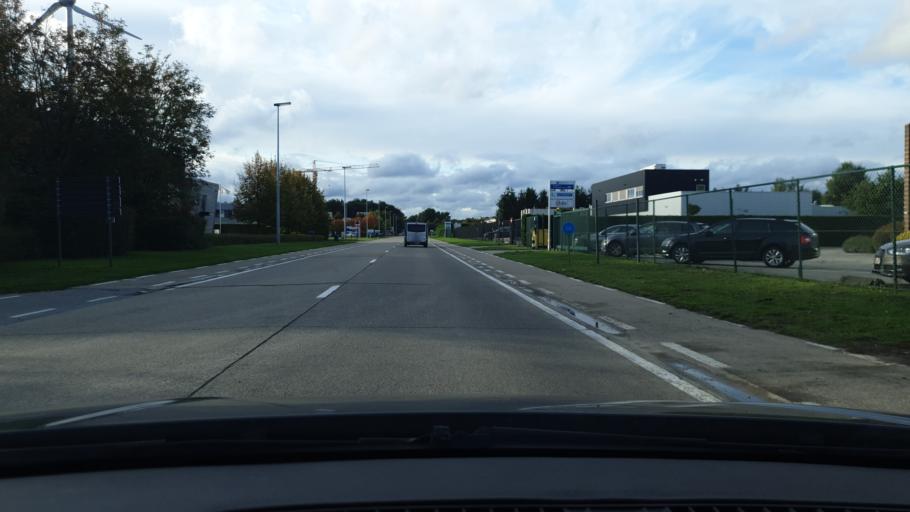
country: BE
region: Flanders
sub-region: Provincie Antwerpen
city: Olen
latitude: 51.1493
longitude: 4.9137
